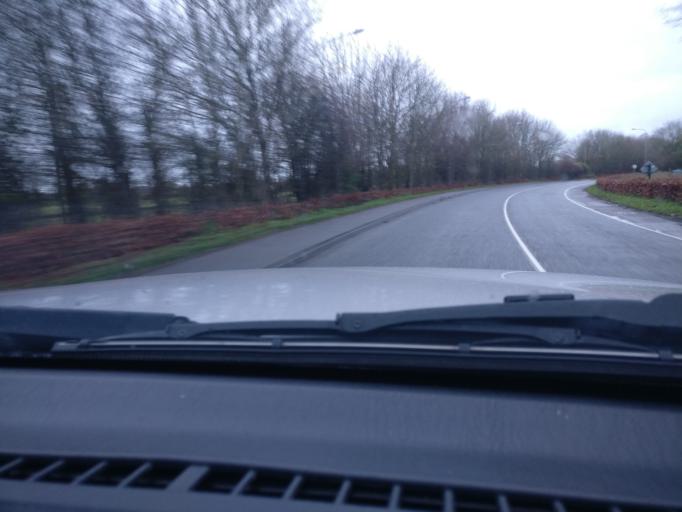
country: IE
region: Leinster
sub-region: An Mhi
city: Trim
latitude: 53.5559
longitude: -6.7819
